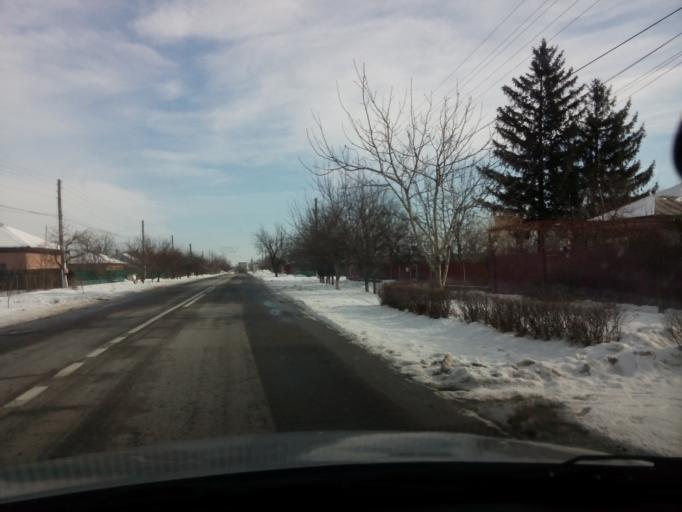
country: RO
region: Calarasi
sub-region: Comuna Soldanu
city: Negoesti
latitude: 44.2314
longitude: 26.4946
